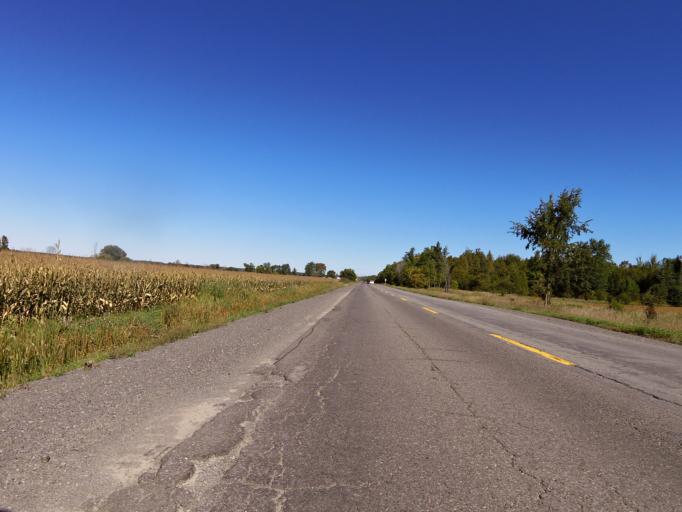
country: CA
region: Ontario
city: Clarence-Rockland
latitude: 45.3888
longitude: -75.4286
